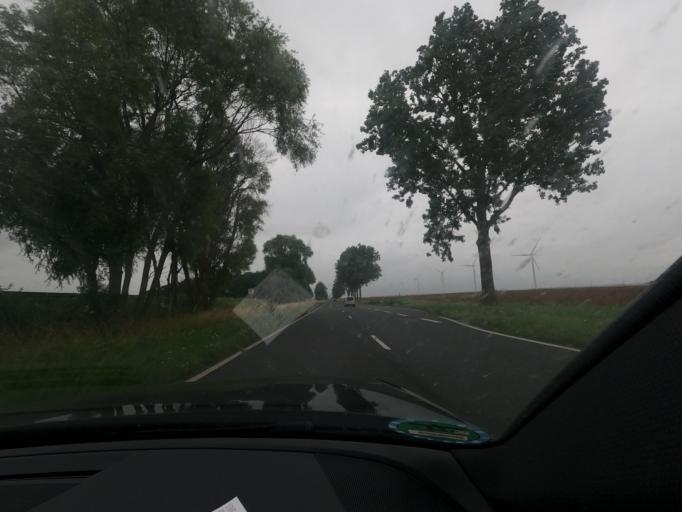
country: FR
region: Picardie
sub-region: Departement de la Somme
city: Roye
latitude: 49.7219
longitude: 2.7328
